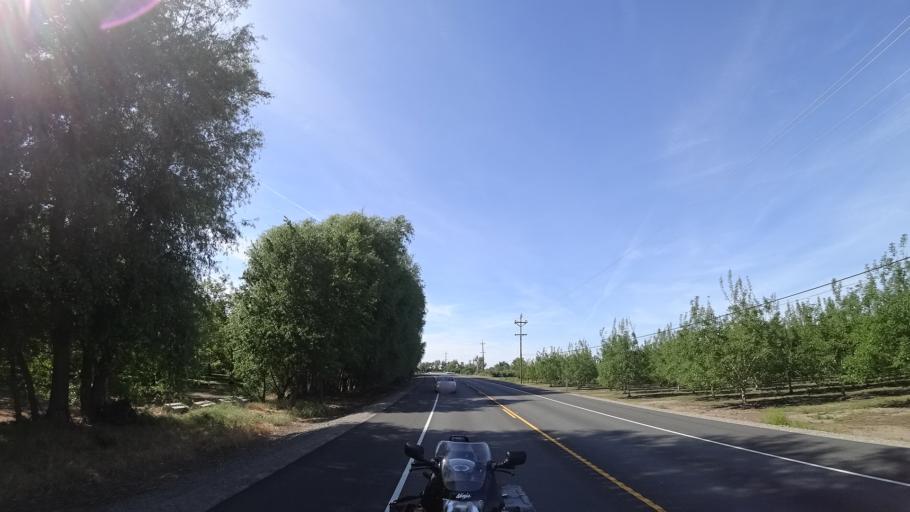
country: US
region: California
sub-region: Glenn County
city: Hamilton City
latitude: 39.8774
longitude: -121.9701
